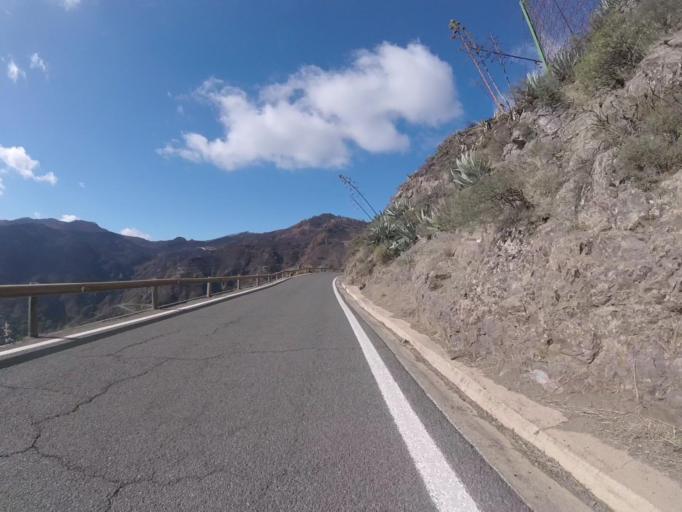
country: ES
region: Canary Islands
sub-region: Provincia de Las Palmas
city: Tejeda
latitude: 28.0095
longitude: -15.5863
